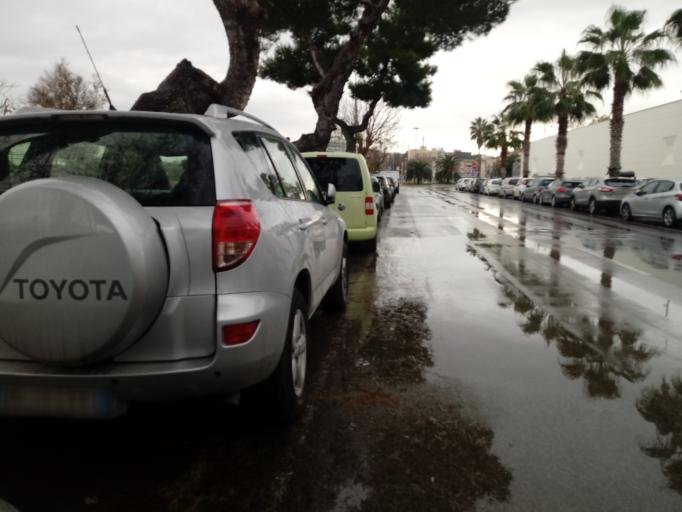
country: IT
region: Apulia
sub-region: Provincia di Bari
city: Bari
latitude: 41.1300
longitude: 16.8501
